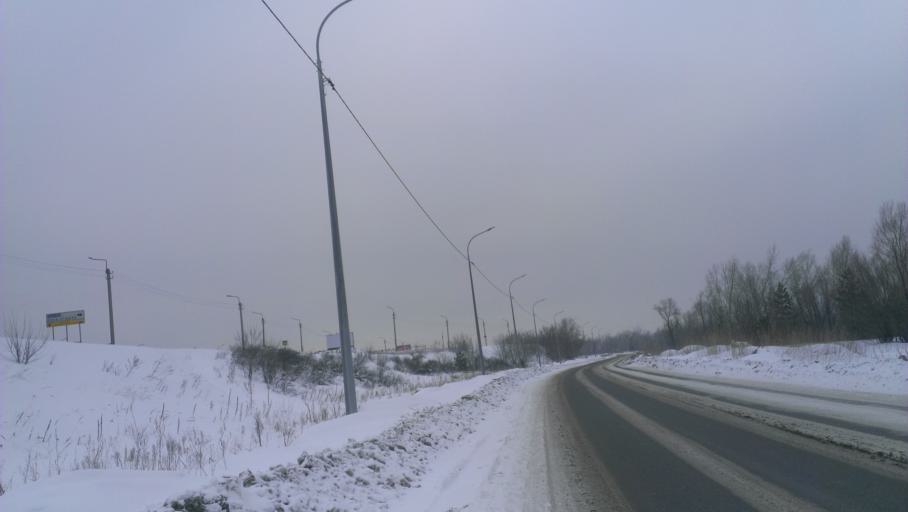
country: RU
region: Altai Krai
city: Zaton
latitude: 53.3188
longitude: 83.8188
